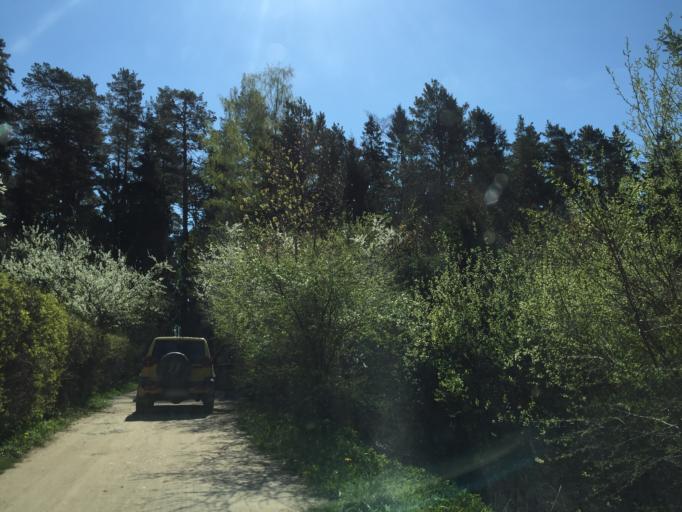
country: LV
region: Saulkrastu
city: Saulkrasti
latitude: 57.3165
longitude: 24.4367
